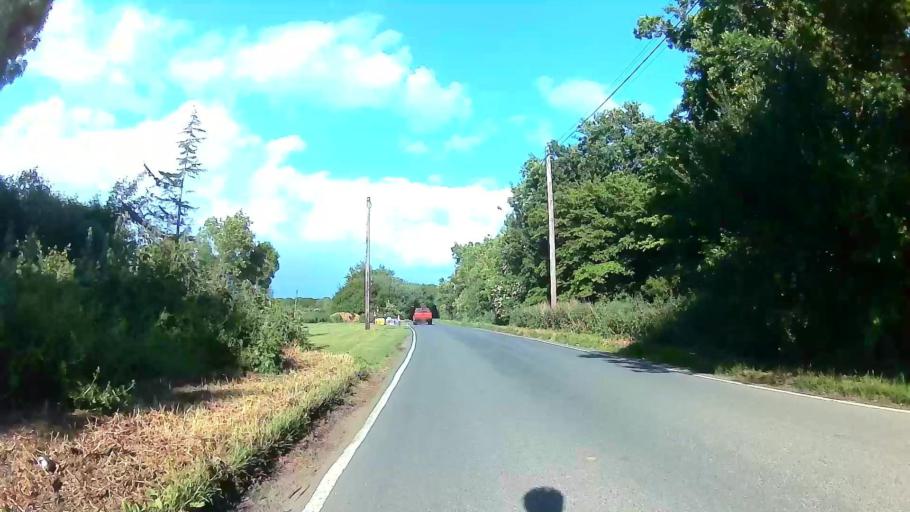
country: GB
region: England
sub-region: Essex
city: Ingatestone
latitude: 51.6943
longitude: 0.3331
